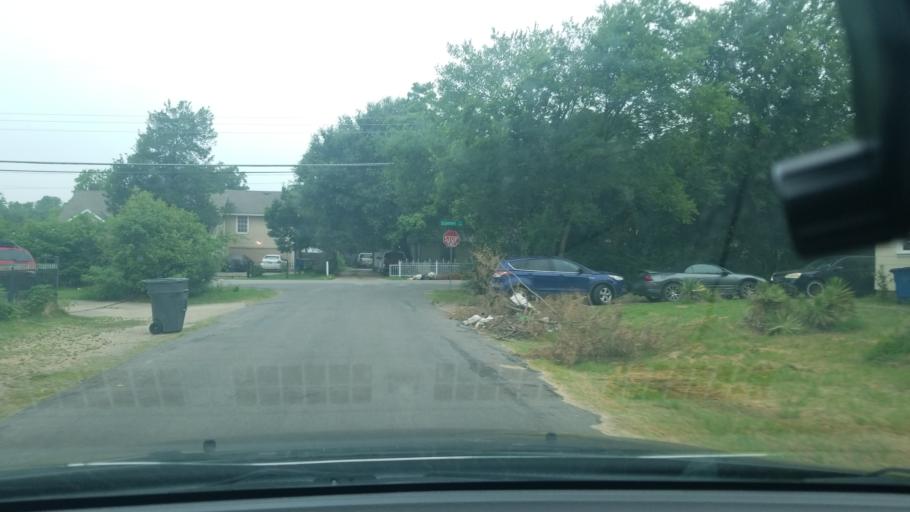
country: US
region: Texas
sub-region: Dallas County
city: Balch Springs
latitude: 32.7558
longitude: -96.6768
